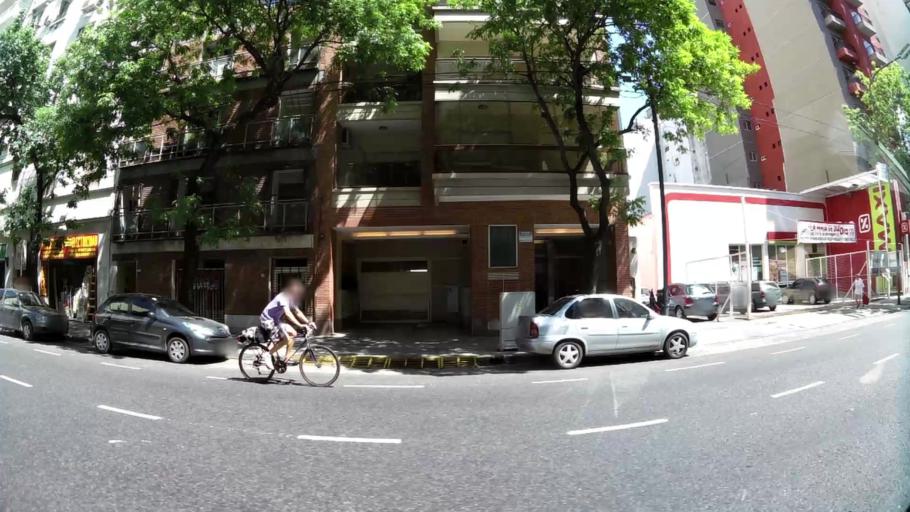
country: AR
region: Buenos Aires F.D.
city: Buenos Aires
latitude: -34.6186
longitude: -58.3983
